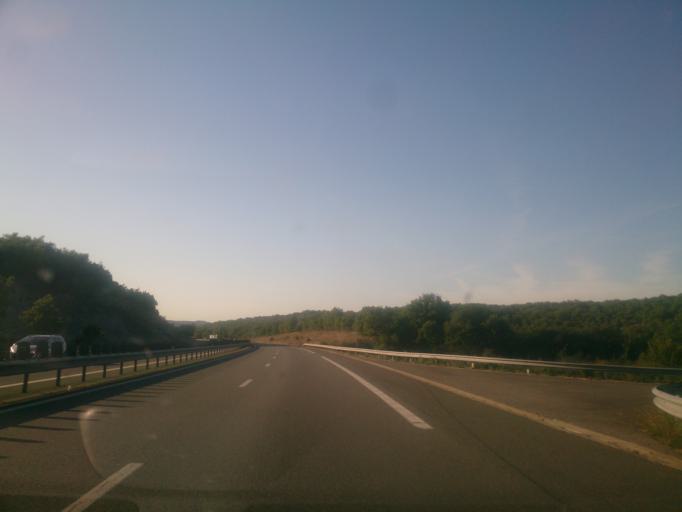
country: FR
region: Midi-Pyrenees
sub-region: Departement du Lot
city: Le Vigan
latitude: 44.7877
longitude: 1.5282
